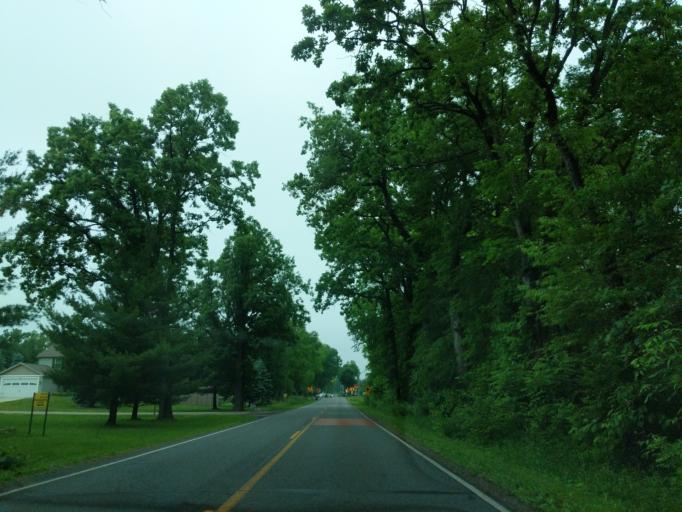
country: US
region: Michigan
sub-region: Jackson County
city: Spring Arbor
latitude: 42.2165
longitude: -84.5410
